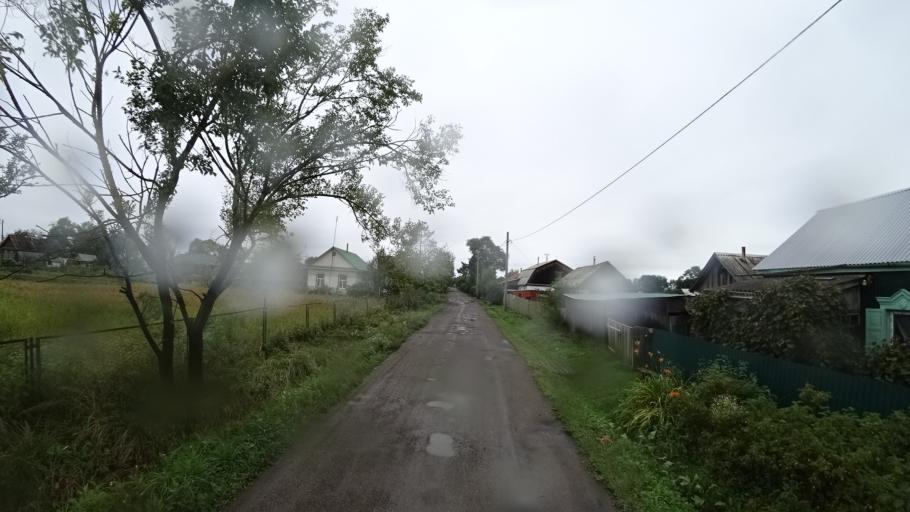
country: RU
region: Primorskiy
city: Monastyrishche
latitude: 44.2033
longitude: 132.4251
